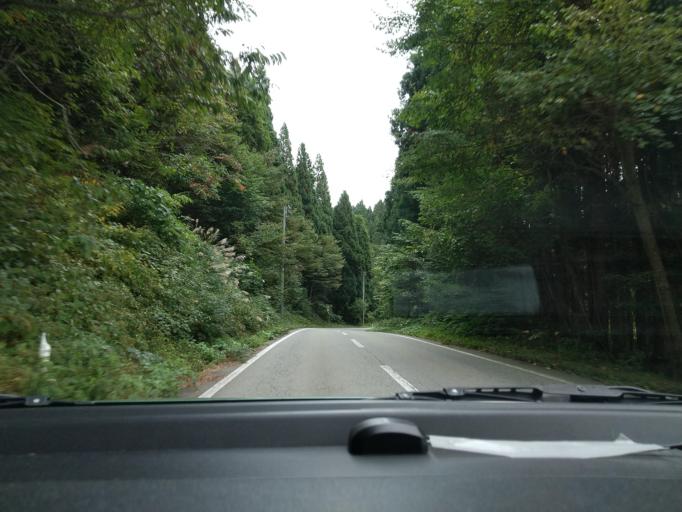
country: JP
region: Akita
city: Kakunodatemachi
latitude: 39.5423
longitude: 140.6396
